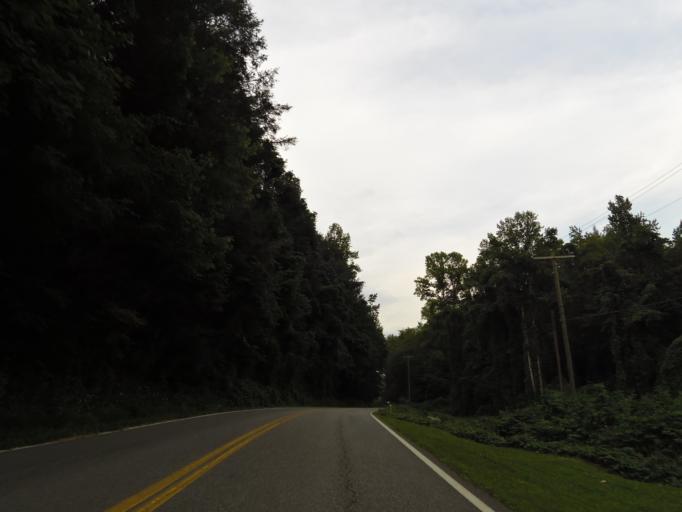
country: US
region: Tennessee
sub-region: Anderson County
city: Rocky Top
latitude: 36.1483
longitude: -84.2062
